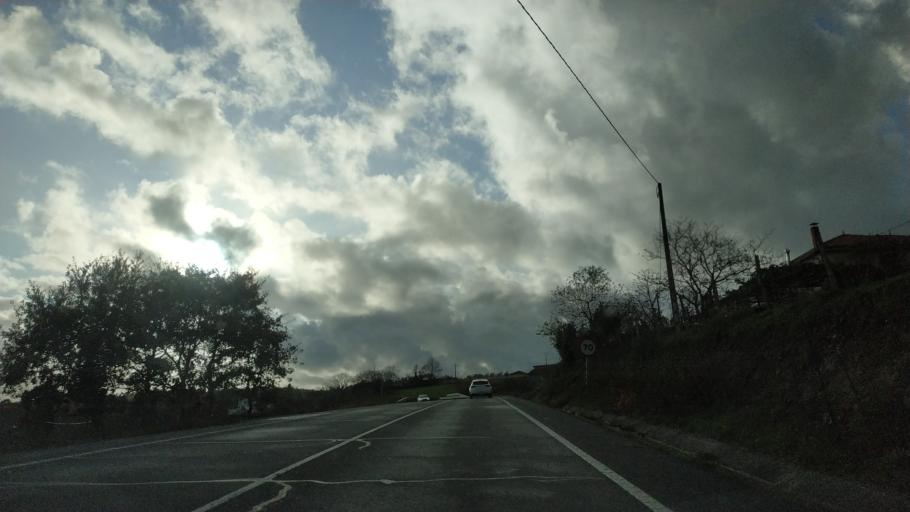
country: ES
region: Galicia
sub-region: Provincia da Coruna
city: Arzua
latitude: 42.8901
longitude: -8.1752
